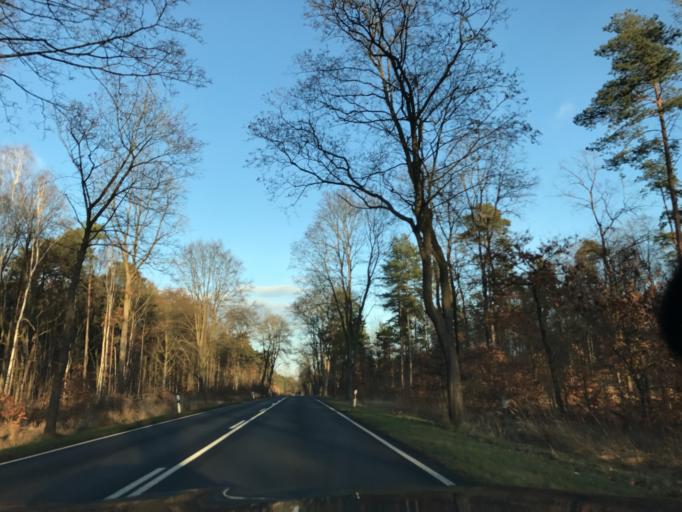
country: DE
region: Saxony-Anhalt
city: Genthin
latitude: 52.3364
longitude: 12.0529
